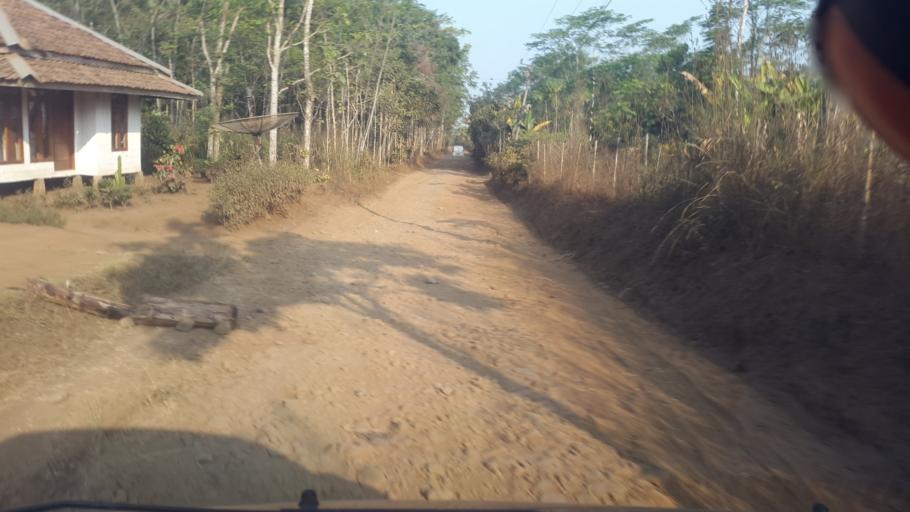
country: ID
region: West Java
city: Sindangraja
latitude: -7.1211
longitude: 106.9340
